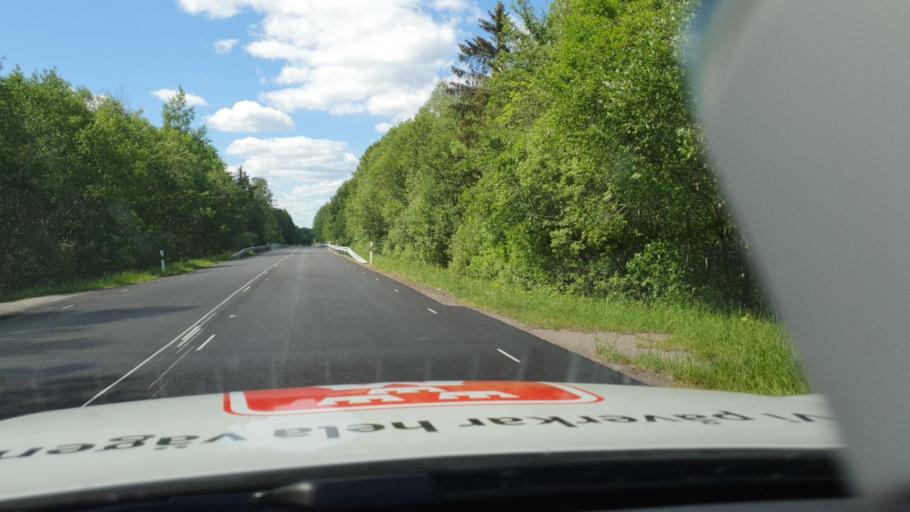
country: SE
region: Uppsala
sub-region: Tierps Kommun
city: Karlholmsbruk
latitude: 60.5162
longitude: 17.6326
